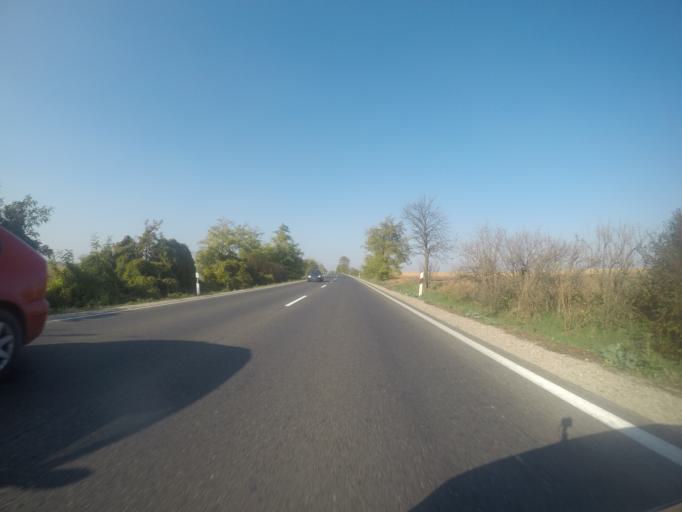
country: HU
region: Fejer
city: Racalmas
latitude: 47.0055
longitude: 18.9306
